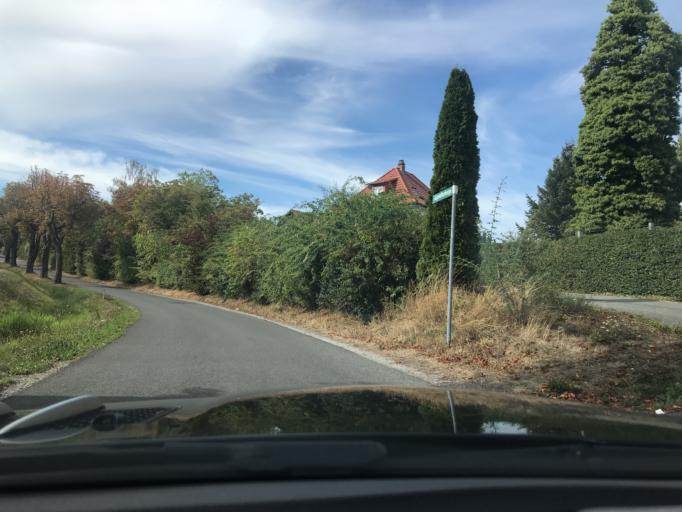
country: DE
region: Thuringia
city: Muehlhausen
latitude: 51.2136
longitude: 10.4453
